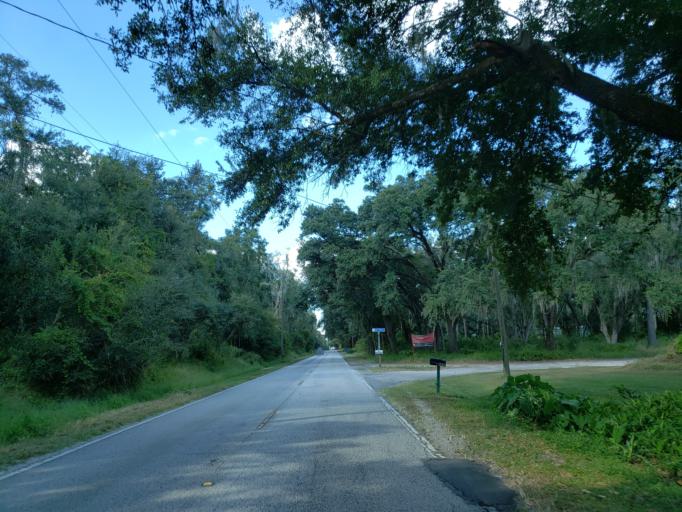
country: US
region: Florida
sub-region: Hillsborough County
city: Valrico
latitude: 27.9435
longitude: -82.2030
